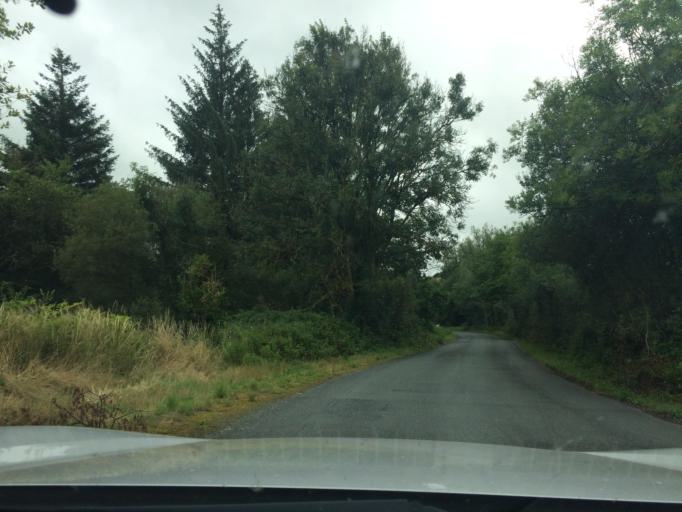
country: IE
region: Munster
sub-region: Waterford
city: Dungarvan
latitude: 52.1961
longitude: -7.7273
